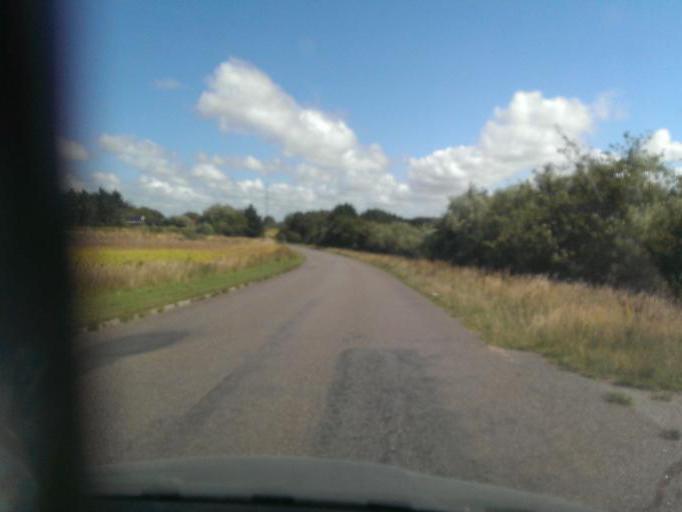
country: DK
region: North Denmark
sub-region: Jammerbugt Kommune
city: Pandrup
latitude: 57.3099
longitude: 9.7088
